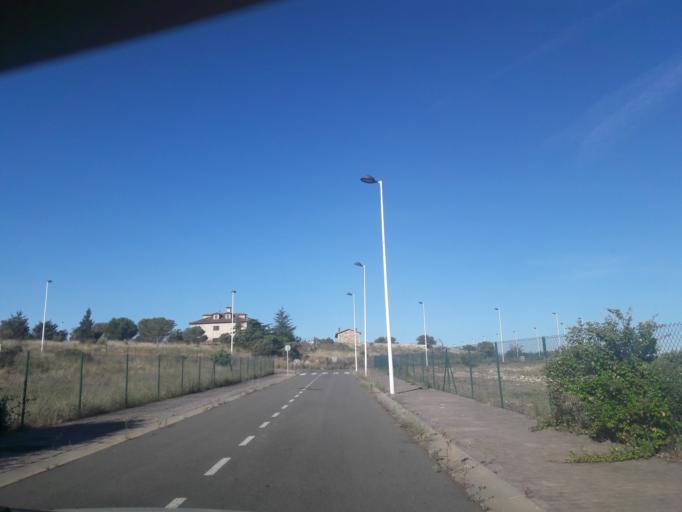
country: ES
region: Castille and Leon
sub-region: Provincia de Salamanca
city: Martinamor
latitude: 40.8087
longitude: -5.6464
